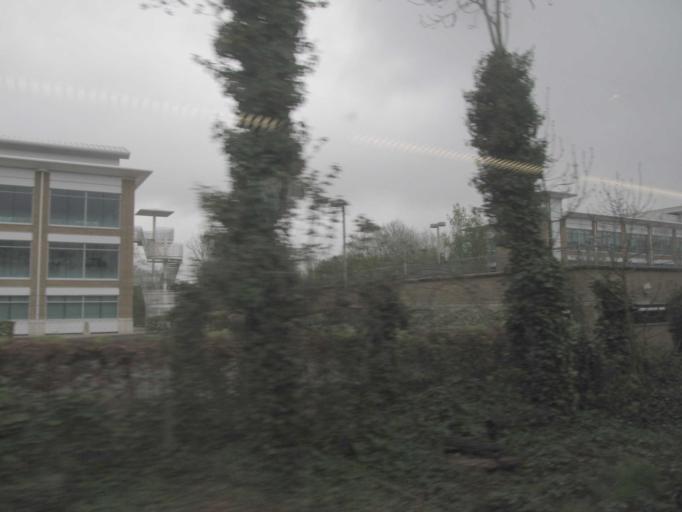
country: GB
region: England
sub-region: Bracknell Forest
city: Sandhurst
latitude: 51.3328
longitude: -0.7786
